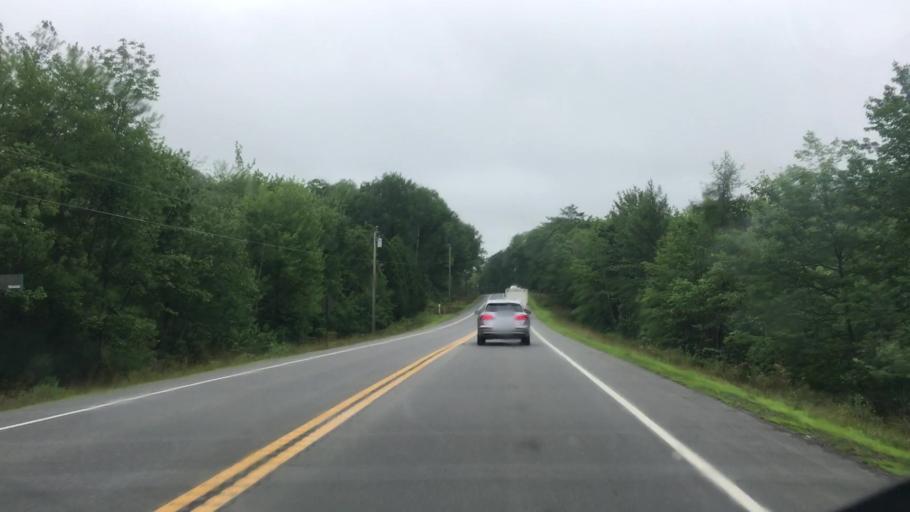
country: US
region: Maine
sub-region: Knox County
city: Washington
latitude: 44.2503
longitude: -69.4072
